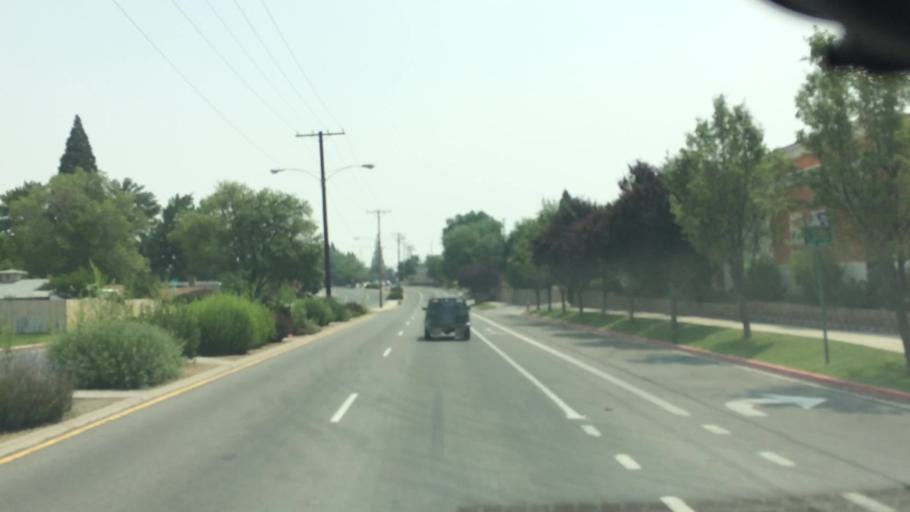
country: US
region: Nevada
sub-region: Washoe County
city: Reno
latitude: 39.5055
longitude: -119.8162
